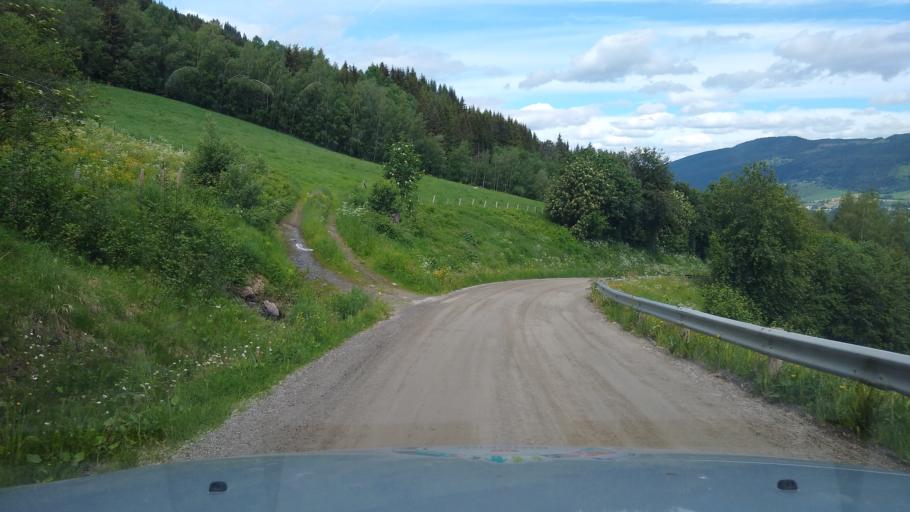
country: NO
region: Oppland
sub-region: Ringebu
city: Ringebu
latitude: 61.5112
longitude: 10.1346
